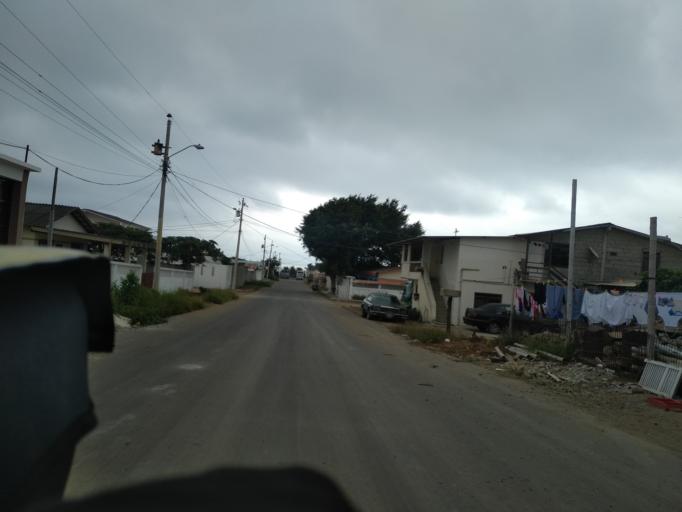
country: EC
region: Santa Elena
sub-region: Canton Santa Elena
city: Santa Elena
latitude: -2.2032
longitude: -80.8697
